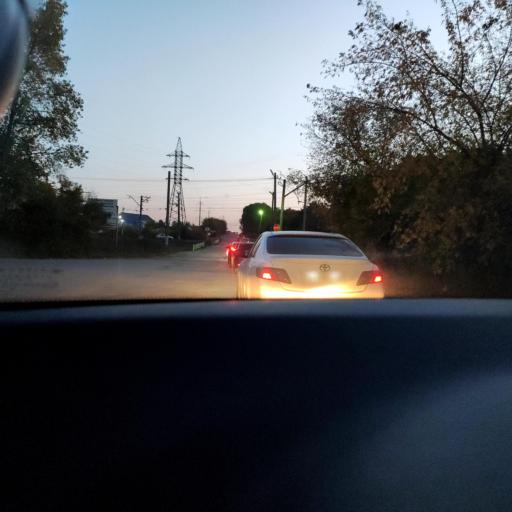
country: RU
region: Samara
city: Novosemeykino
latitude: 53.3360
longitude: 50.3208
